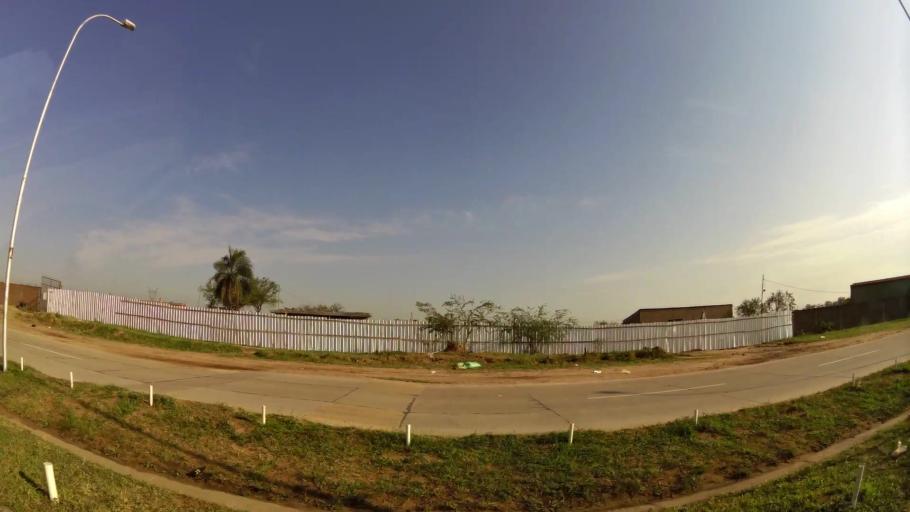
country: BO
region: Santa Cruz
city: Santa Cruz de la Sierra
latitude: -17.6816
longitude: -63.1486
